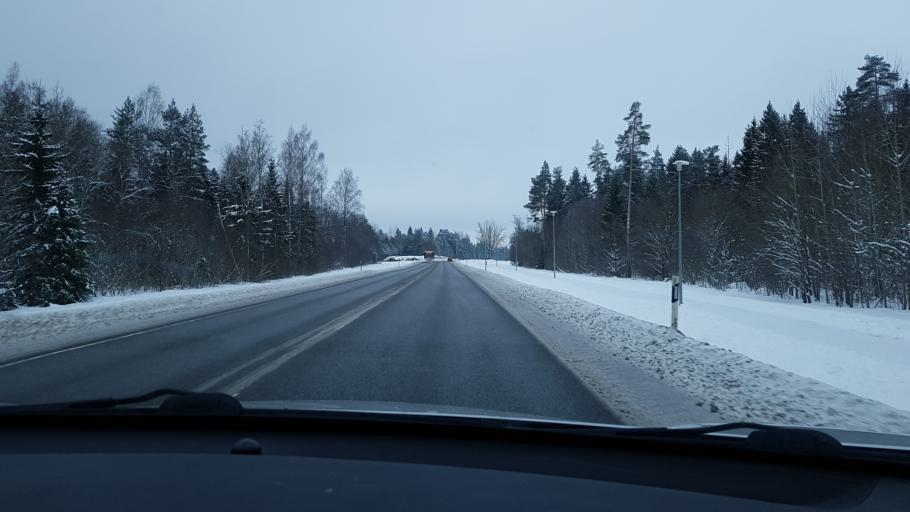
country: EE
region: Jaervamaa
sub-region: Paide linn
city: Paide
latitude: 58.8701
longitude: 25.4947
